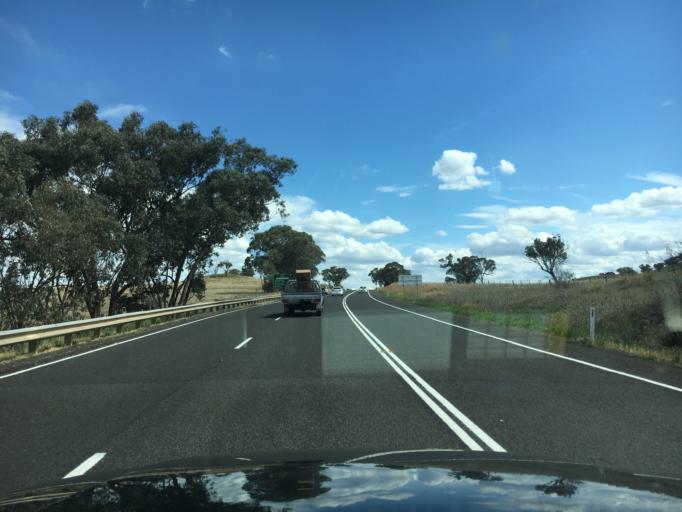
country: AU
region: New South Wales
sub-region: Liverpool Plains
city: Quirindi
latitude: -31.4977
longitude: 150.8648
